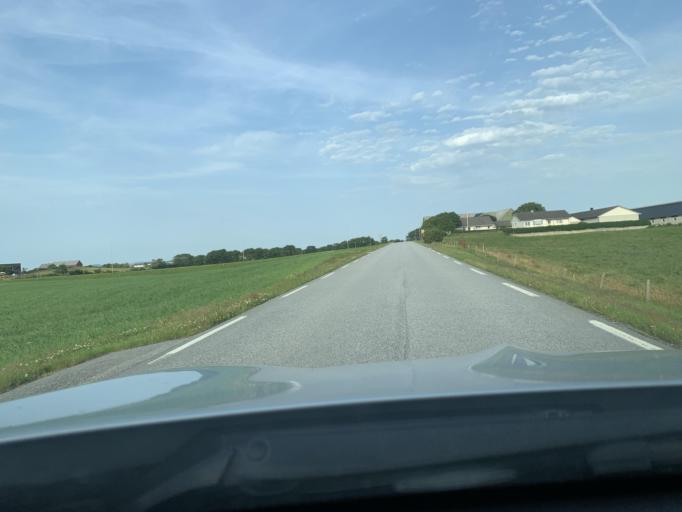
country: NO
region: Rogaland
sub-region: Klepp
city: Kleppe
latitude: 58.7190
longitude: 5.5604
